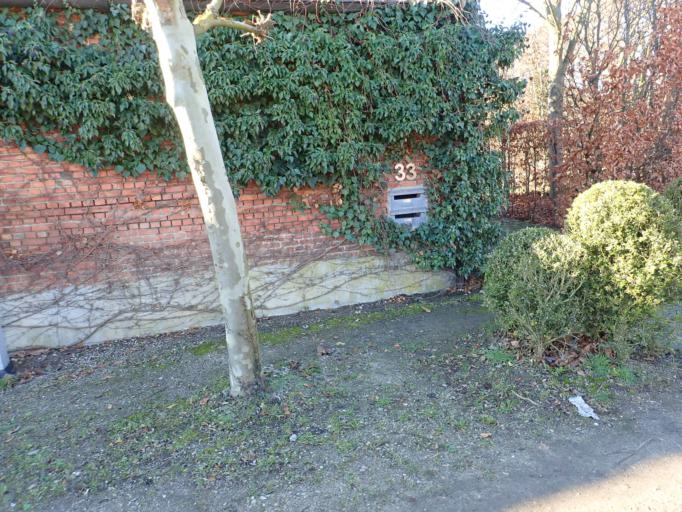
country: BE
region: Flanders
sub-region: Provincie Antwerpen
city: Nijlen
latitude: 51.1524
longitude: 4.6354
